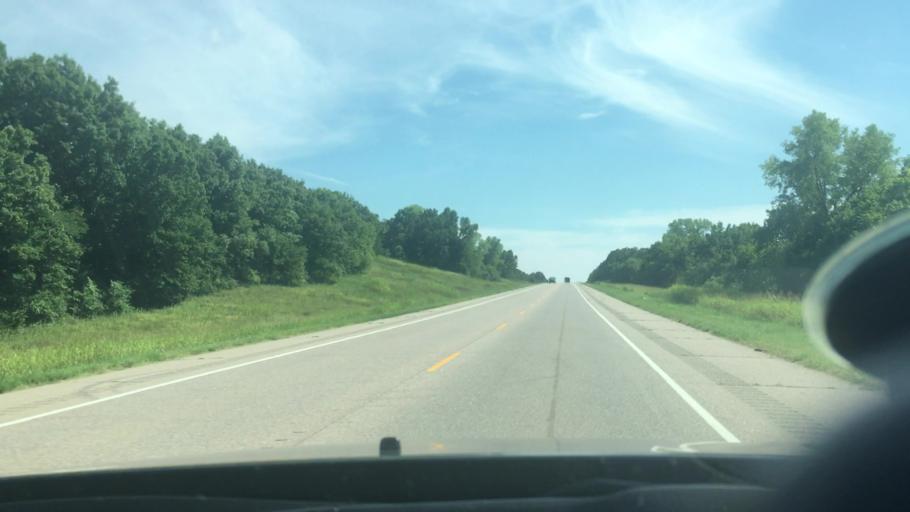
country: US
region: Oklahoma
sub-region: Seminole County
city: Maud
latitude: 35.1091
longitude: -96.6789
